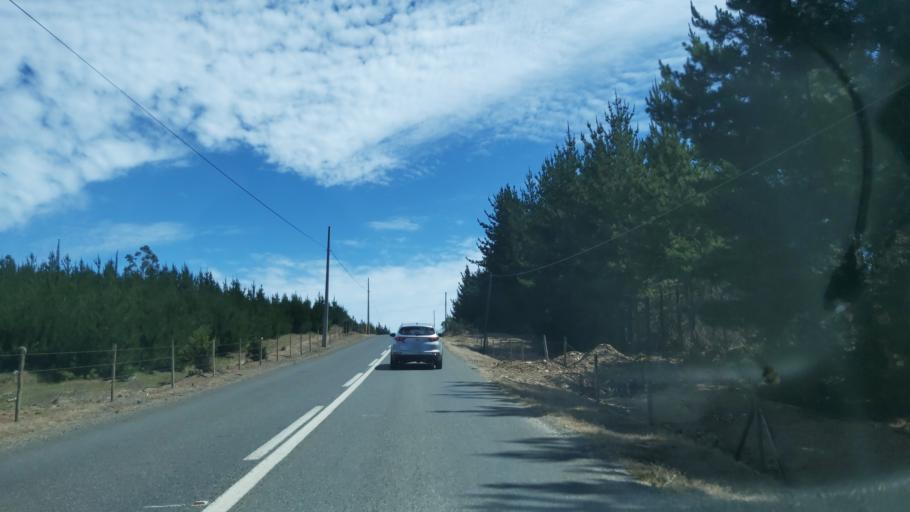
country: CL
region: Maule
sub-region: Provincia de Talca
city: Constitucion
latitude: -35.5229
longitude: -72.5363
